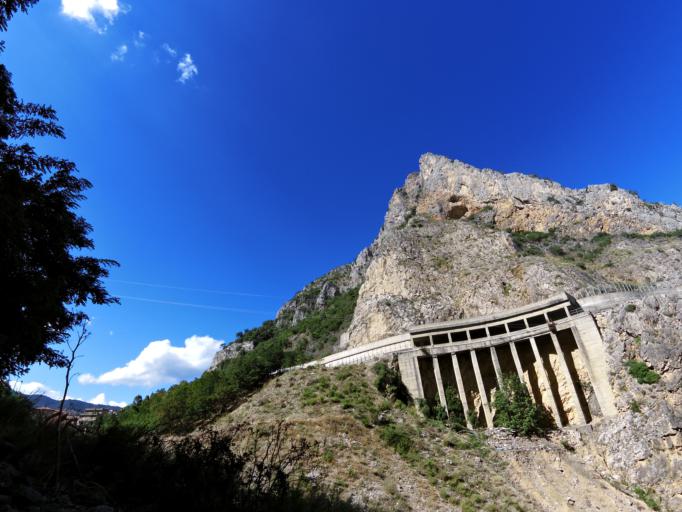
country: IT
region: Calabria
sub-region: Provincia di Reggio Calabria
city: Pazzano
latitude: 38.4724
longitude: 16.4550
